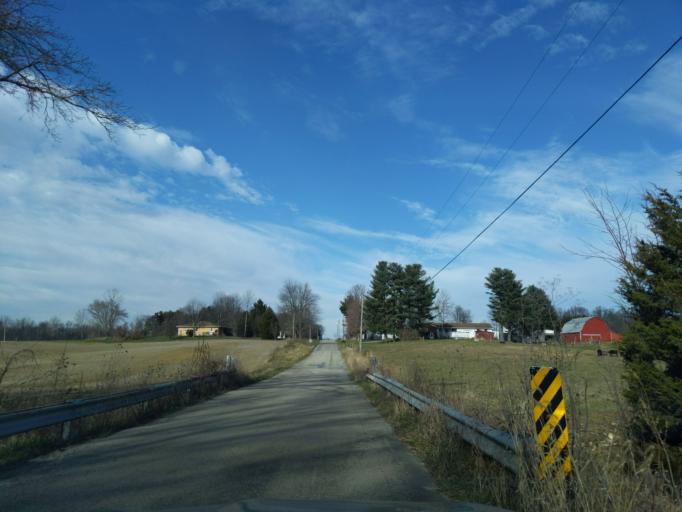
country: US
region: Indiana
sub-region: Decatur County
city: Greensburg
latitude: 39.2839
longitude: -85.4235
